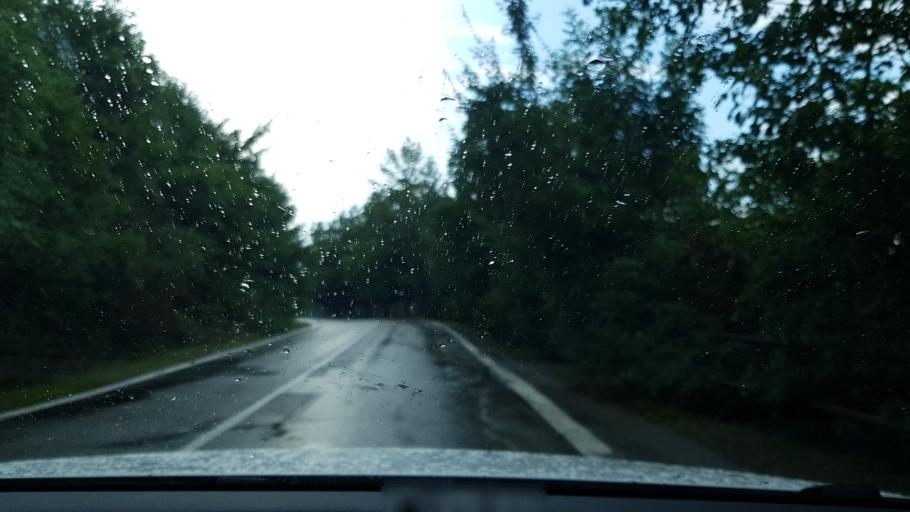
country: SK
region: Trenciansky
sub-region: Okres Povazska Bystrica
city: Povazska Bystrica
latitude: 49.1088
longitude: 18.4522
